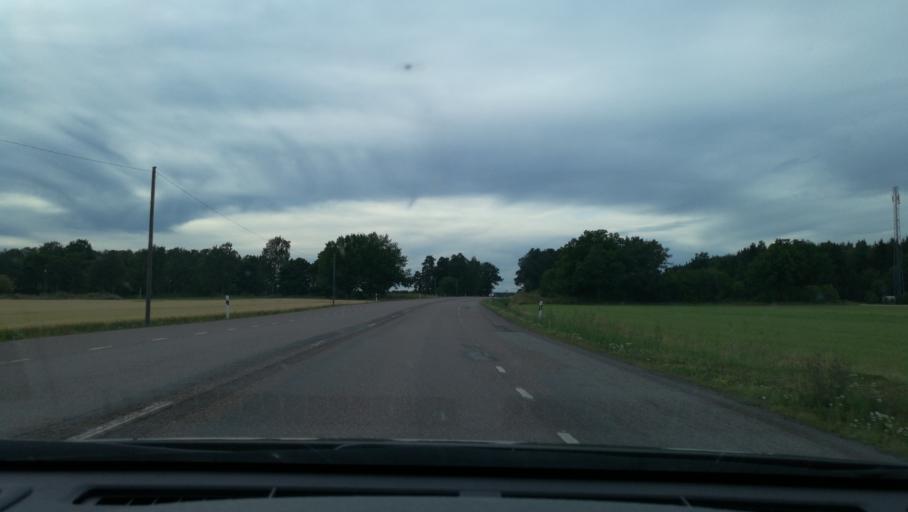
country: SE
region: Vaestmanland
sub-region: Kopings Kommun
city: Koping
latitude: 59.4641
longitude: 15.9963
